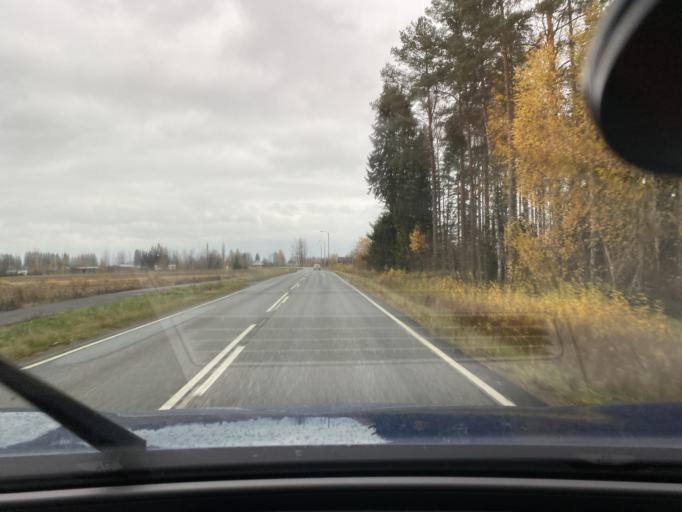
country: FI
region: Satakunta
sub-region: Rauma
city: Saekylae
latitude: 61.0618
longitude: 22.4951
